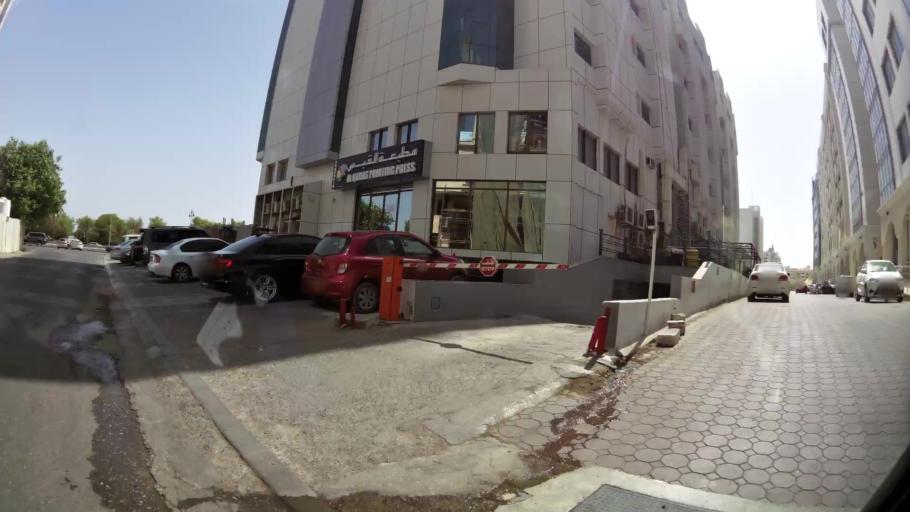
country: OM
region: Muhafazat Masqat
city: Bawshar
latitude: 23.5961
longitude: 58.4182
